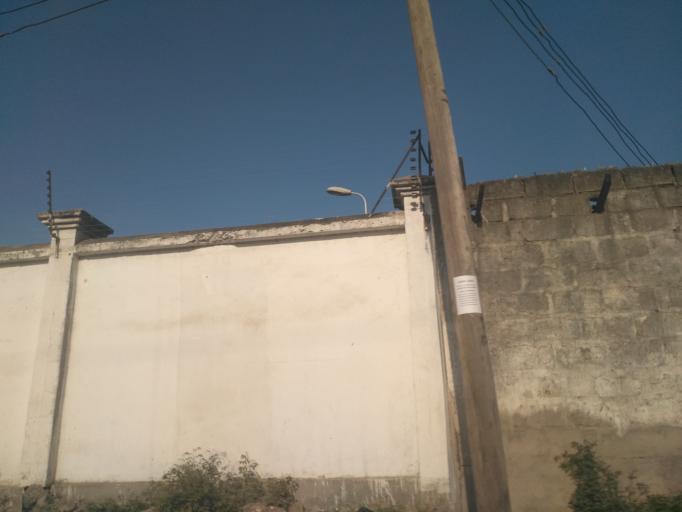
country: TZ
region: Pwani
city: Vikindu
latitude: -6.9182
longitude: 39.2659
